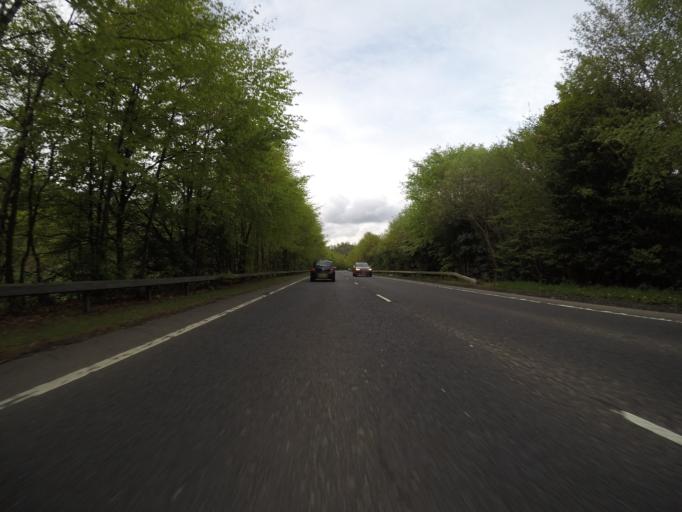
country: GB
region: Scotland
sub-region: West Dunbartonshire
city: Balloch
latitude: 56.0645
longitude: -4.6458
